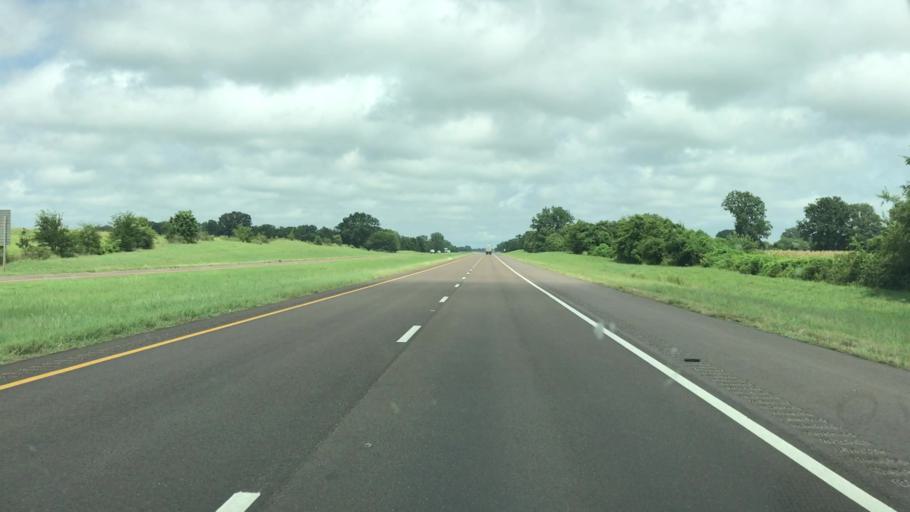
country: US
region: Tennessee
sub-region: Dyer County
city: Dyersburg
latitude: 36.0809
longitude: -89.3361
